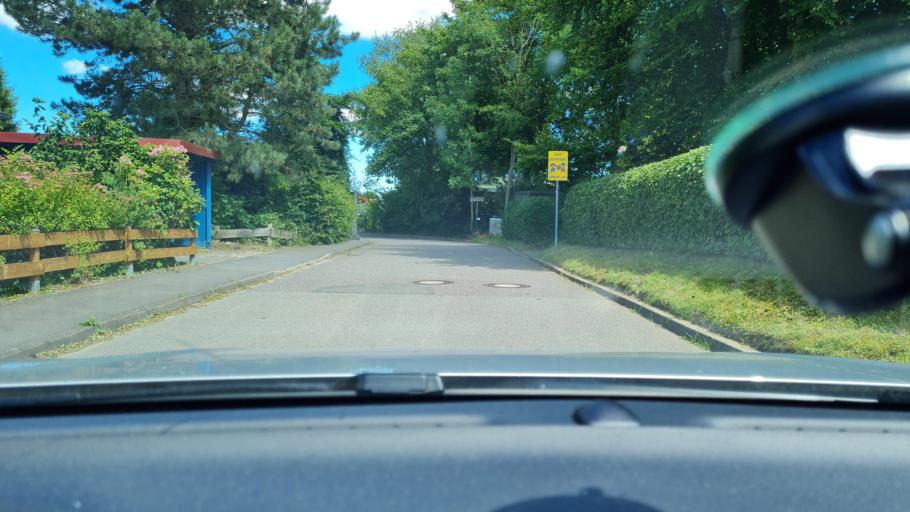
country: DE
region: Schleswig-Holstein
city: Rabenkirchen-Fauluck
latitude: 54.5929
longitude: 9.8669
